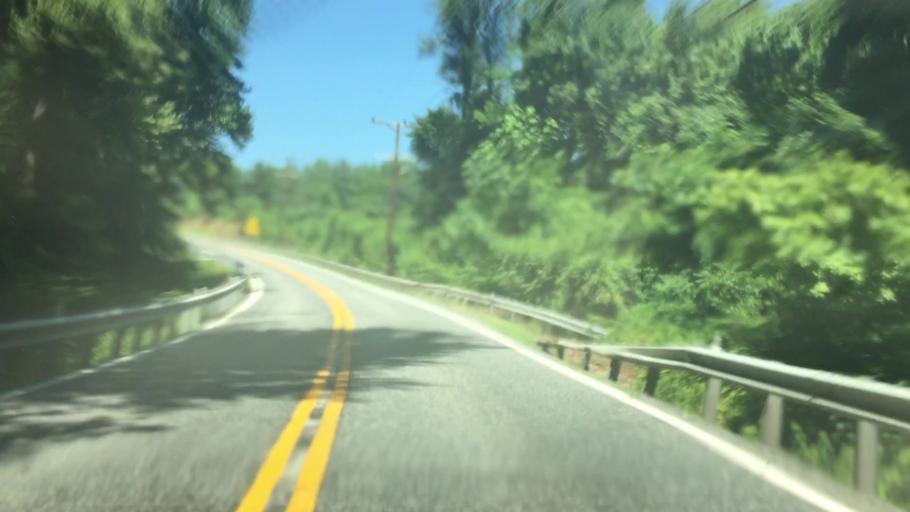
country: US
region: Maryland
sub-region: Harford County
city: Aberdeen
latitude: 39.5936
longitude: -76.1872
